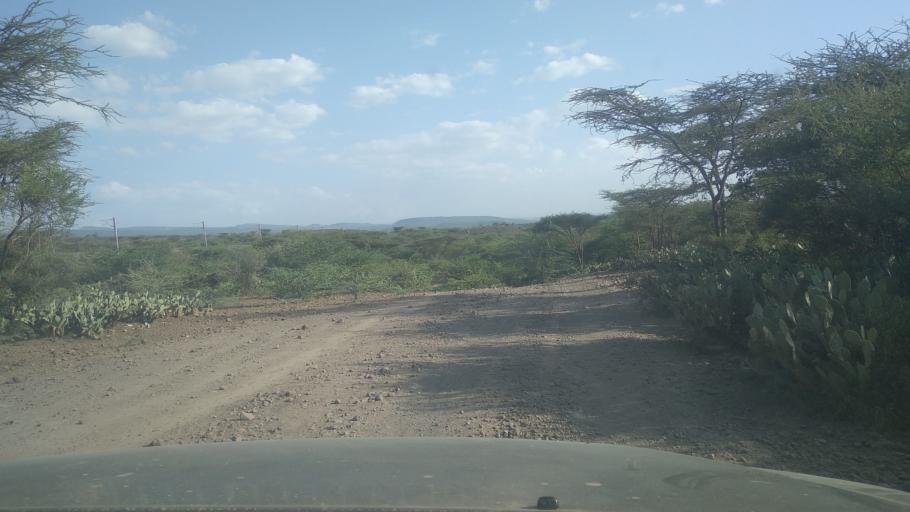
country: ET
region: Oromiya
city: Hirna
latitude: 9.4505
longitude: 40.9897
